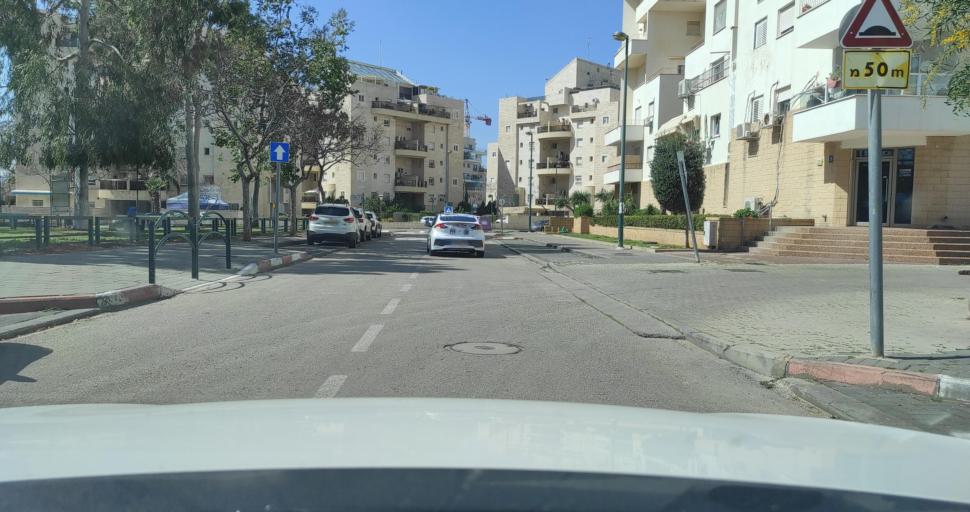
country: IL
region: Central District
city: Nordiyya
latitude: 32.3086
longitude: 34.8720
